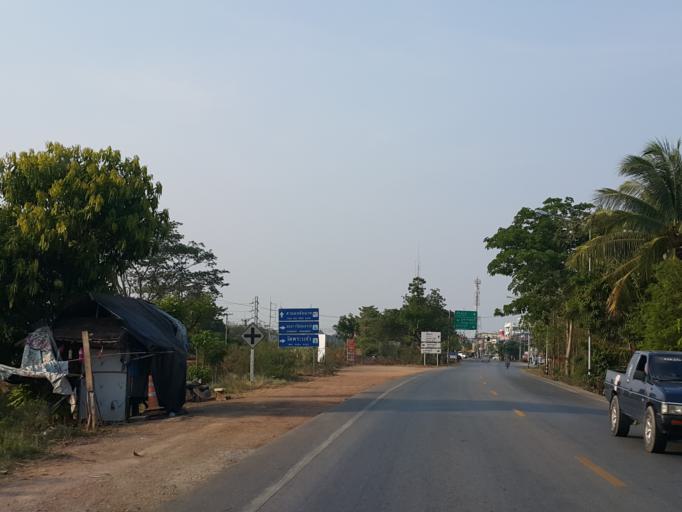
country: TH
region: Chai Nat
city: Sankhaburi
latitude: 15.0416
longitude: 100.1476
